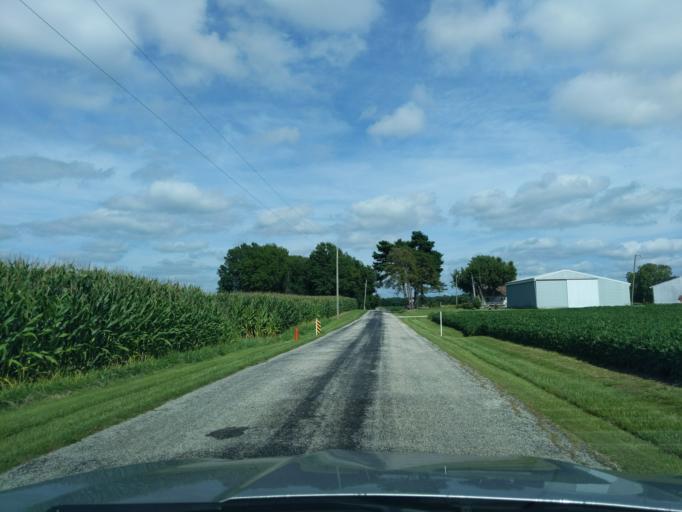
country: US
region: Indiana
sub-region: Decatur County
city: Greensburg
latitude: 39.2349
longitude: -85.3877
